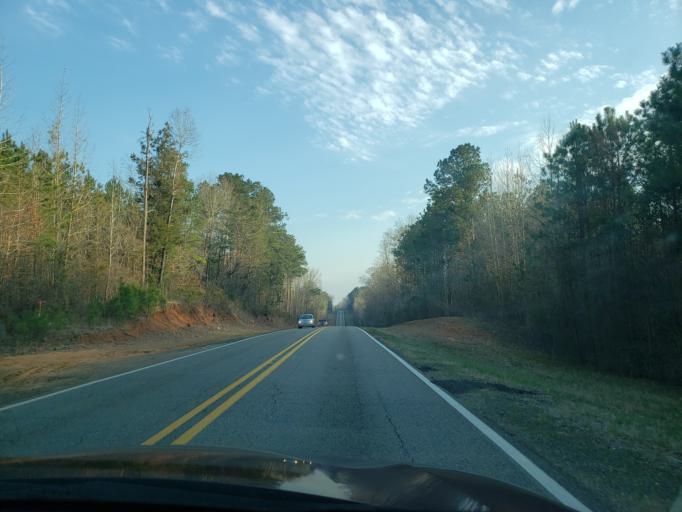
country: US
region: Alabama
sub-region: Hale County
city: Greensboro
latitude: 32.7910
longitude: -87.5905
